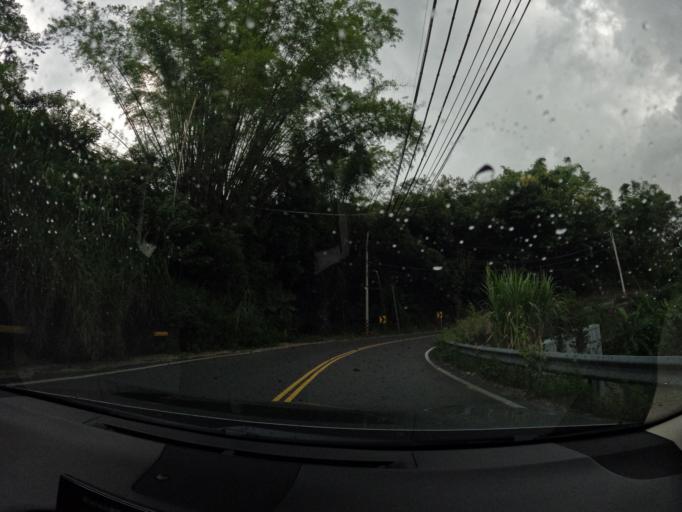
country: TW
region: Taiwan
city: Lugu
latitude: 23.8363
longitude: 120.7736
